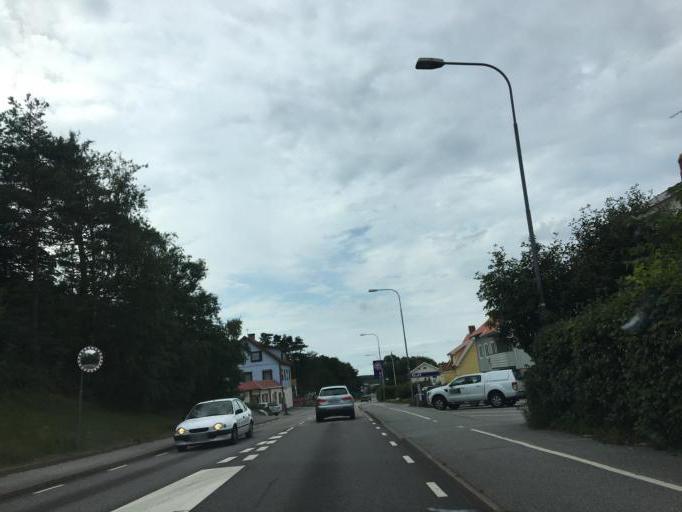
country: SE
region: Vaestra Goetaland
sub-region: Sotenas Kommun
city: Hunnebostrand
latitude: 58.4390
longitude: 11.3036
